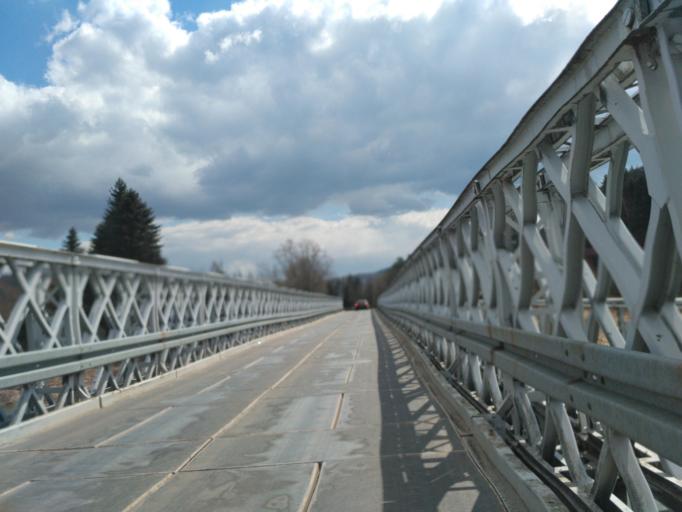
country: PL
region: Subcarpathian Voivodeship
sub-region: Powiat sanocki
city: Sanok
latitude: 49.6144
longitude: 22.2715
